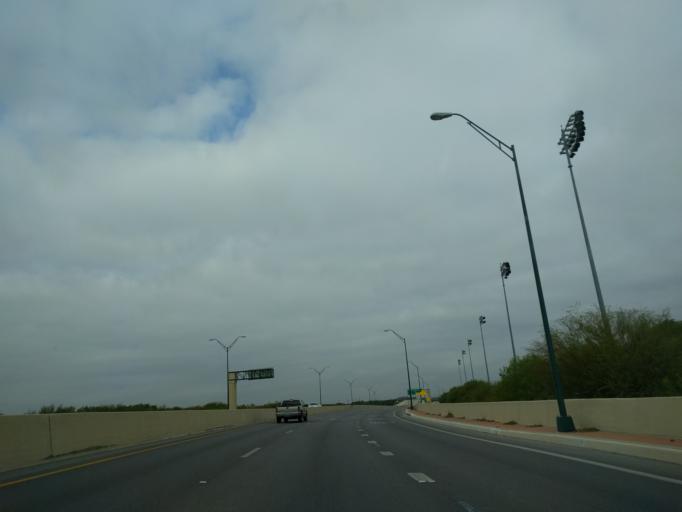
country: US
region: Texas
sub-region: Bexar County
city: Castle Hills
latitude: 29.5447
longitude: -98.4672
